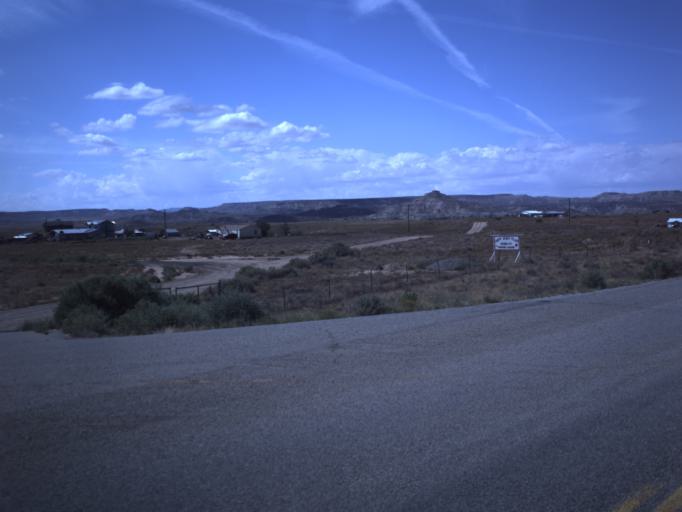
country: US
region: Colorado
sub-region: Montezuma County
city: Towaoc
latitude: 37.1779
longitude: -109.1194
